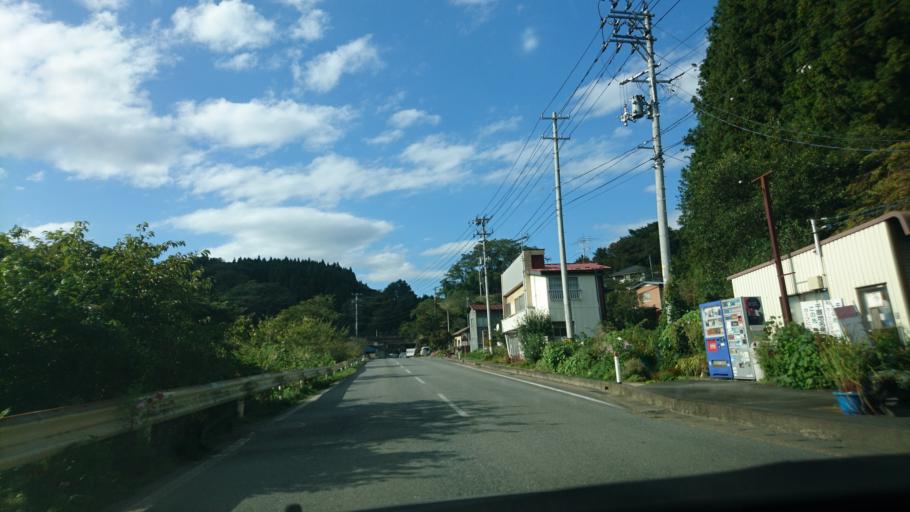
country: JP
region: Iwate
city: Ichinoseki
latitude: 38.9013
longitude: 141.3251
